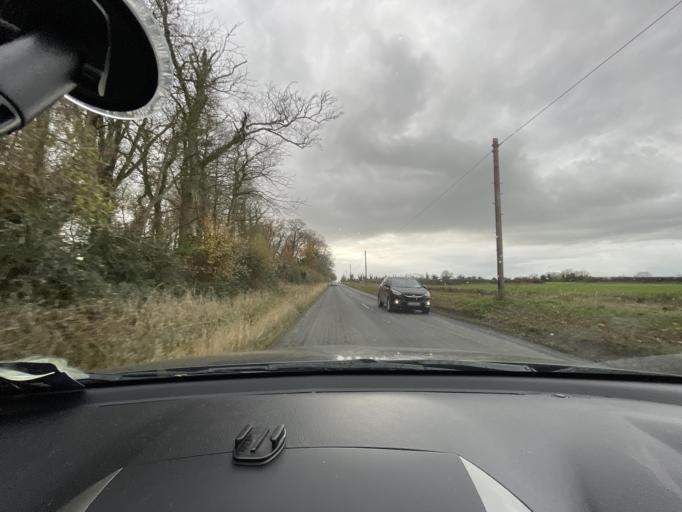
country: IE
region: Leinster
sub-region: Lu
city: Drogheda
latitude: 53.7339
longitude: -6.3144
